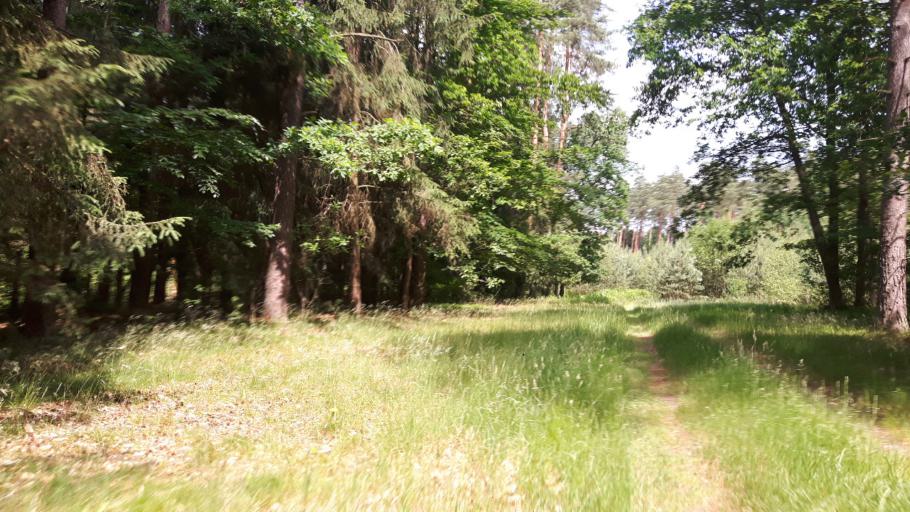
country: PL
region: West Pomeranian Voivodeship
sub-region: Powiat goleniowski
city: Goleniow
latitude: 53.6177
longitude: 14.8776
